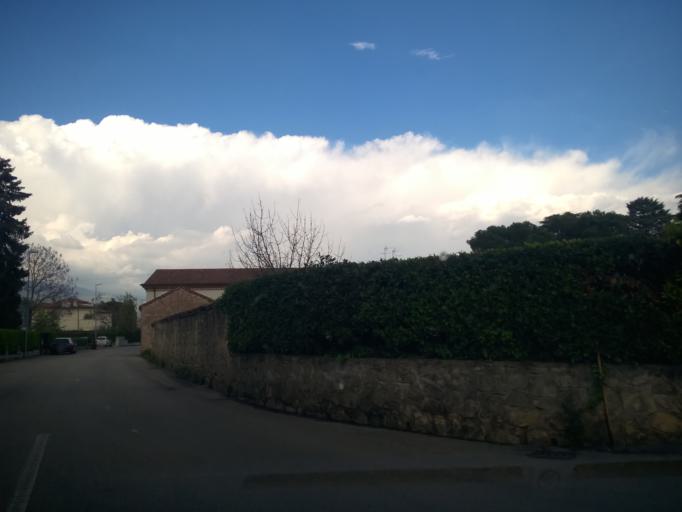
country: IT
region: Veneto
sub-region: Provincia di Vicenza
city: Thiene
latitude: 45.7105
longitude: 11.4781
